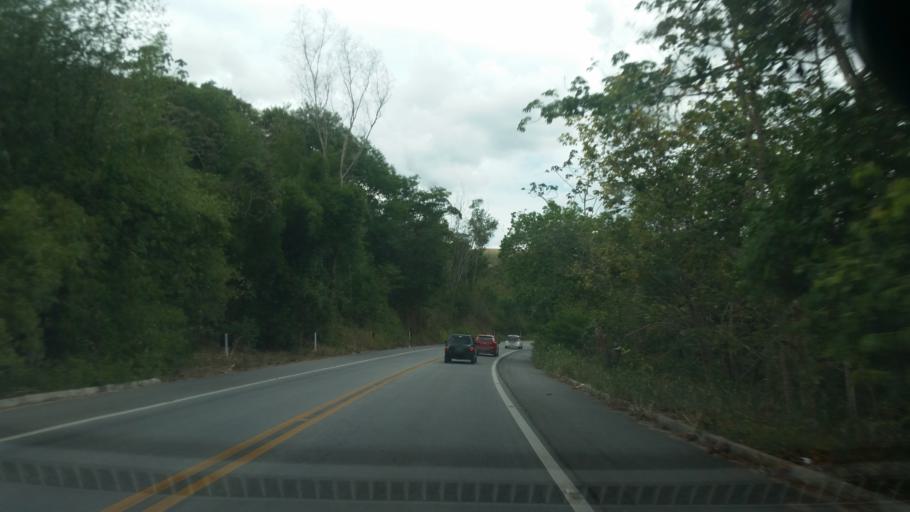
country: BR
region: Alagoas
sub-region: Uniao Dos Palmares
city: Uniao dos Palmares
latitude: -9.1947
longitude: -36.0323
